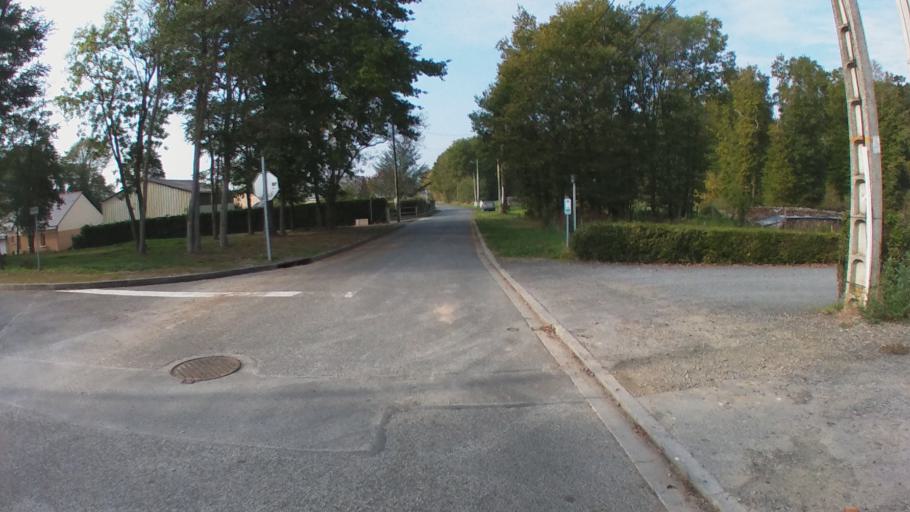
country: FR
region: Pays de la Loire
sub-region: Departement de Maine-et-Loire
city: Distre
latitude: 47.2429
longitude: -0.1163
